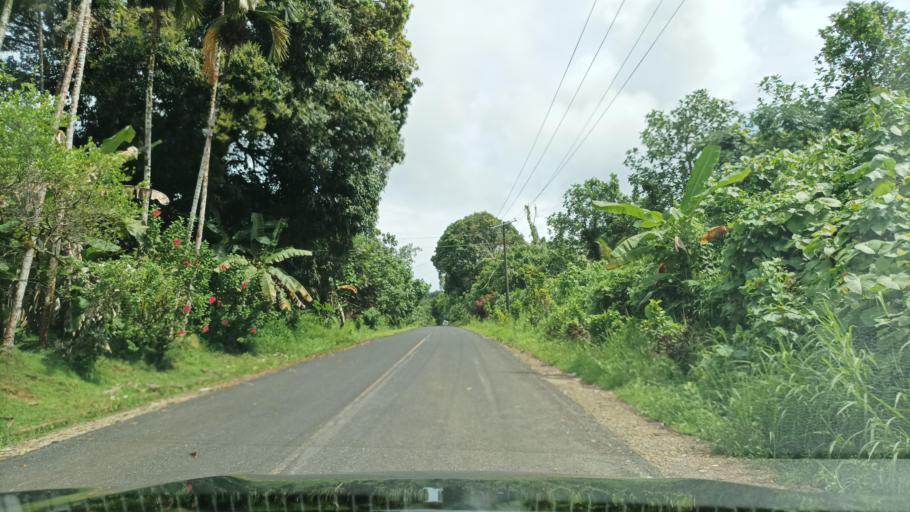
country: FM
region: Pohnpei
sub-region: Madolenihm Municipality
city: Madolenihm Municipality Government
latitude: 6.8823
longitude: 158.2900
